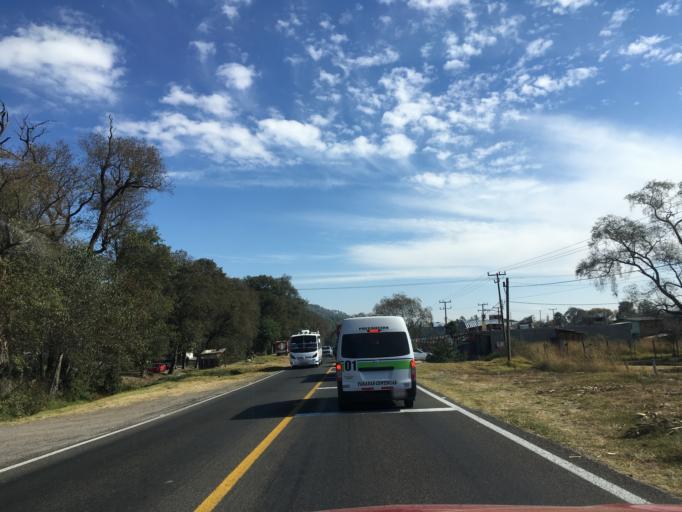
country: MX
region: Michoacan
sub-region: Hidalgo
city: San Lucas Huarirapeo (La Mesa de San Lucas)
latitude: 19.6713
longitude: -100.6670
